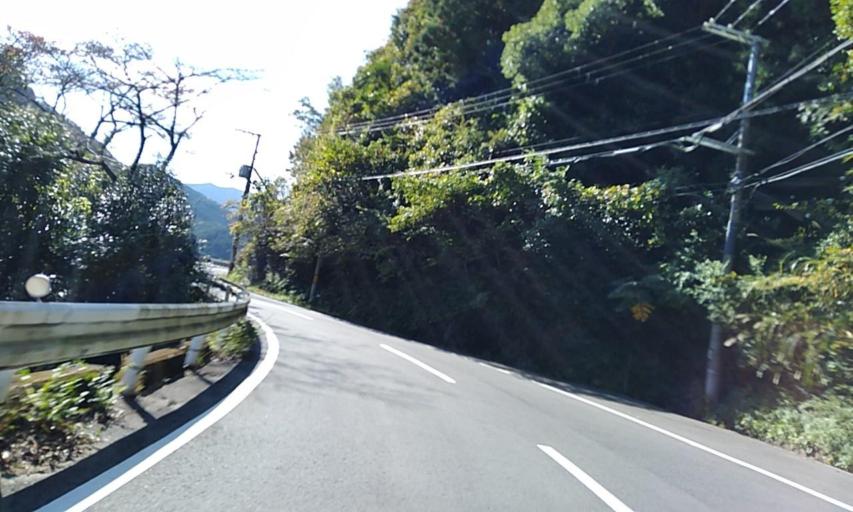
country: JP
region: Wakayama
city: Kainan
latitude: 34.0819
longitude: 135.3577
